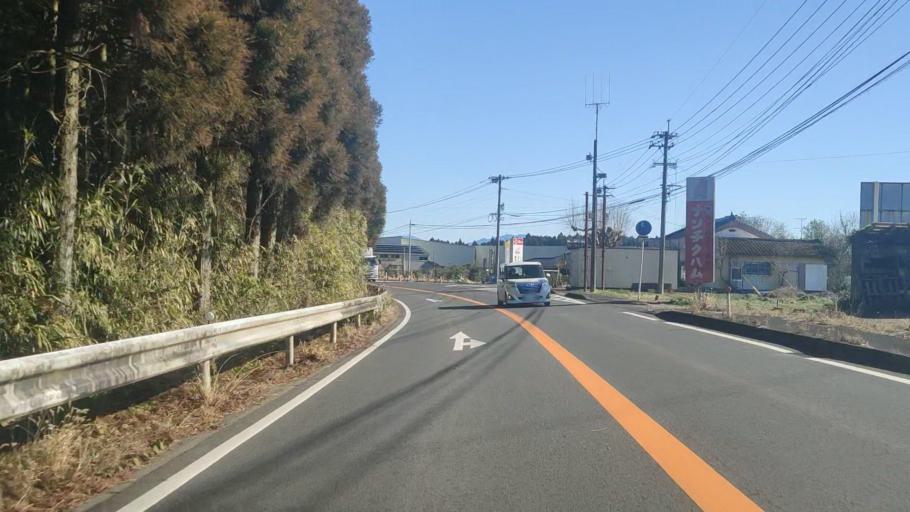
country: JP
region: Kagoshima
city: Sueyoshicho-ninokata
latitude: 31.6941
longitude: 130.9838
